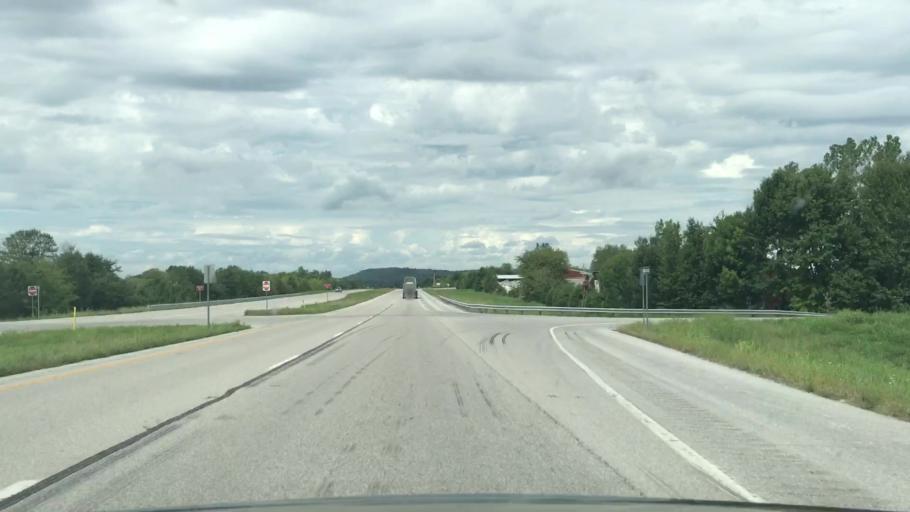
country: US
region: Kentucky
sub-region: Todd County
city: Elkton
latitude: 36.8299
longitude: -87.2259
